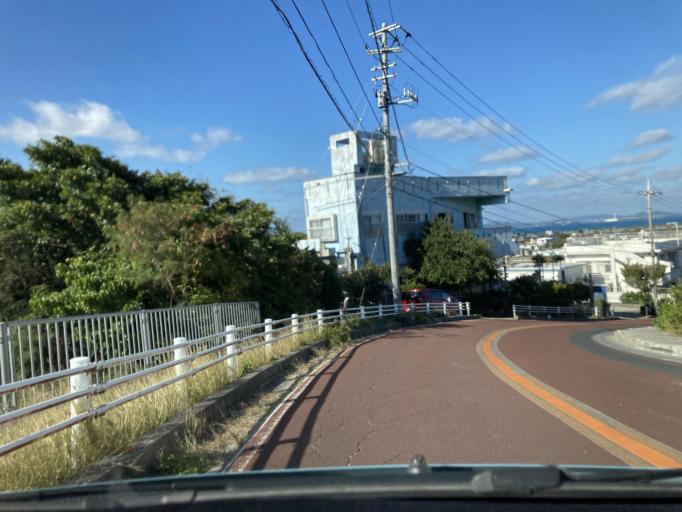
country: JP
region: Okinawa
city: Katsuren-haebaru
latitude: 26.3194
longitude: 127.9093
